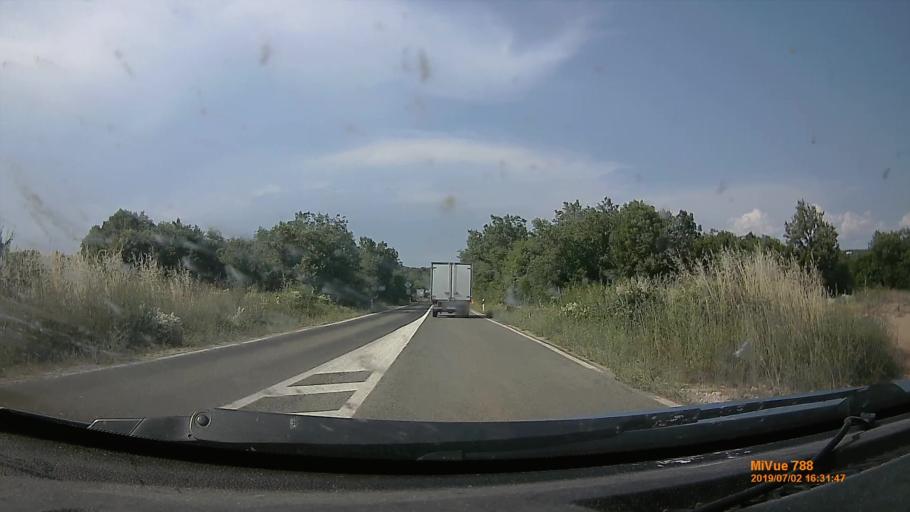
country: HR
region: Primorsko-Goranska
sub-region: Grad Krk
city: Krk
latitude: 45.0573
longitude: 14.4875
